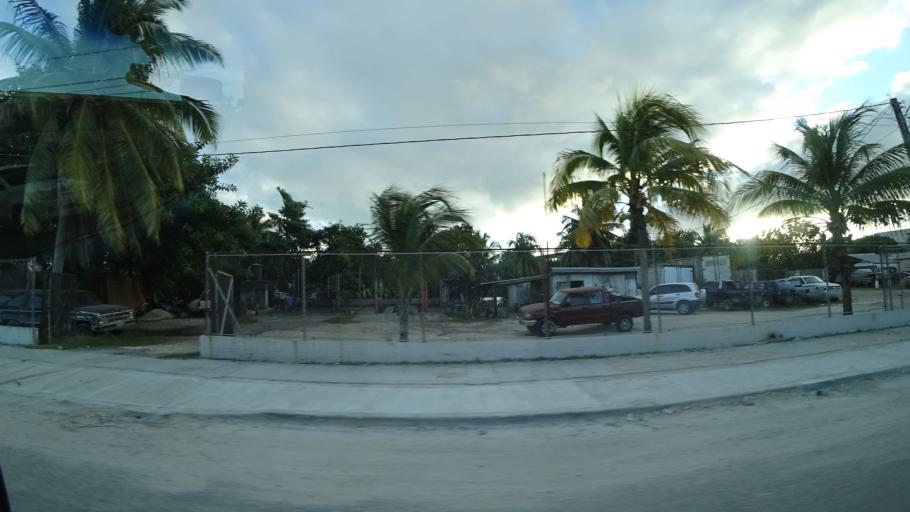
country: BZ
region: Belize
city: Belize City
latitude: 17.5104
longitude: -88.2115
